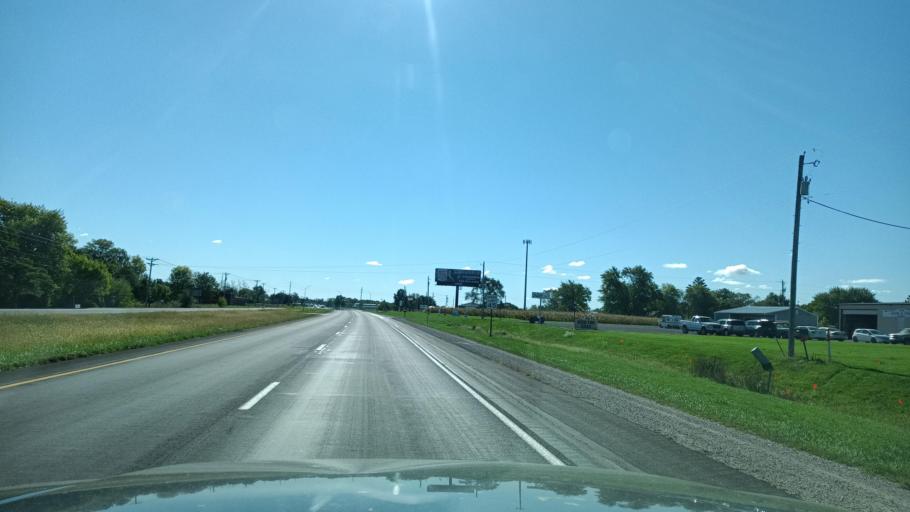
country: US
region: Iowa
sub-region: Lee County
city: Keokuk
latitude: 40.4394
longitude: -91.4308
